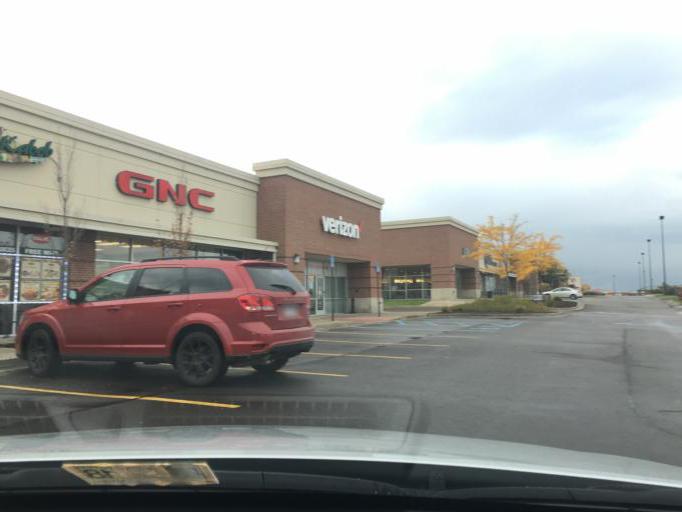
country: US
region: Michigan
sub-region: Wayne County
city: Allen Park
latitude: 42.2834
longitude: -83.2052
